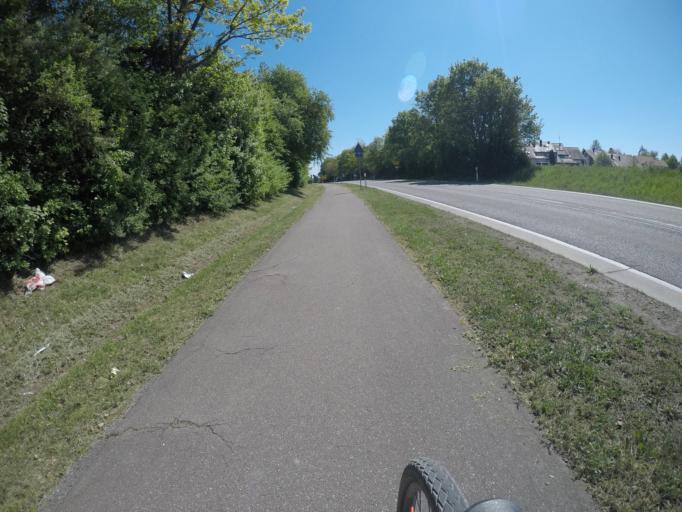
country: DE
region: Baden-Wuerttemberg
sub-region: Regierungsbezirk Stuttgart
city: Waiblingen
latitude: 48.8574
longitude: 9.2924
